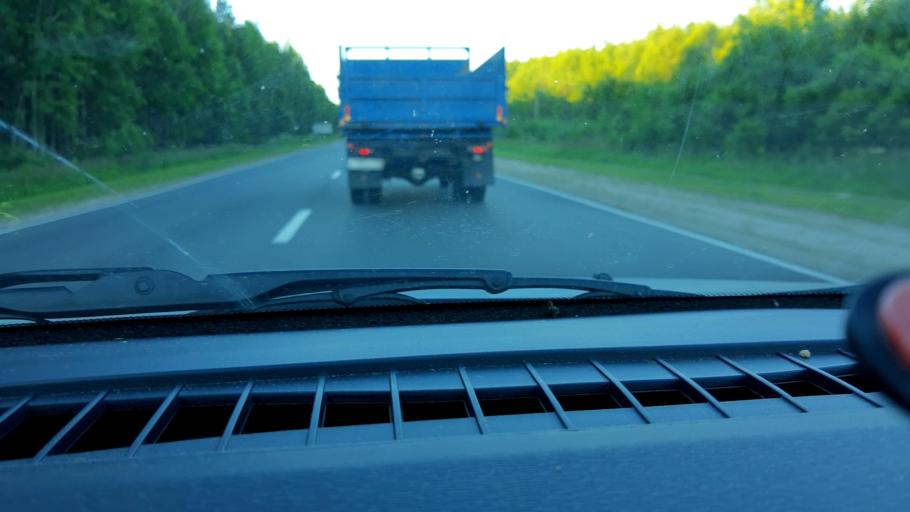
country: RU
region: Nizjnij Novgorod
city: Semenov
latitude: 56.8133
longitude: 44.4769
